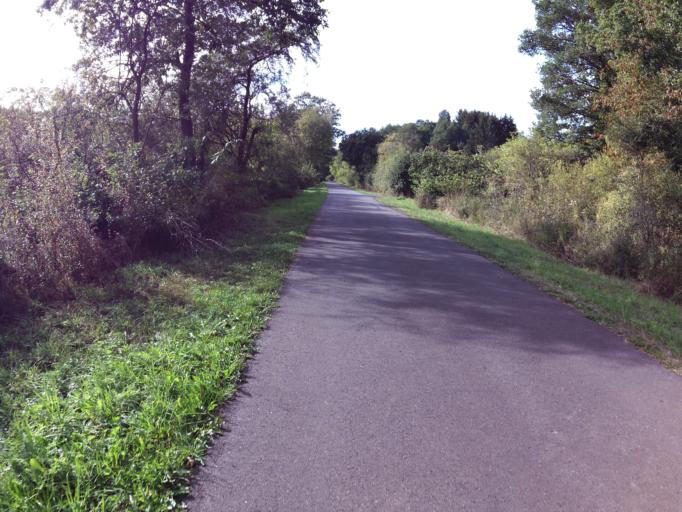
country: DE
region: Rheinland-Pfalz
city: Winterspelt
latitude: 50.2247
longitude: 6.2164
